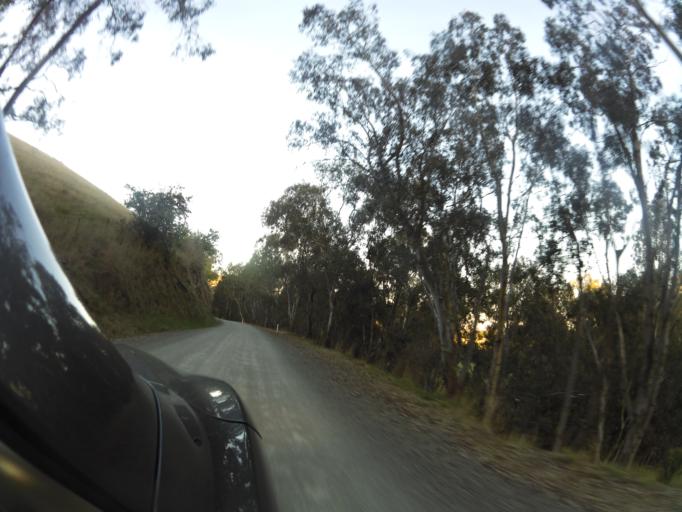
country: AU
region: Victoria
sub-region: Murrindindi
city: Alexandra
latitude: -37.1535
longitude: 145.5377
